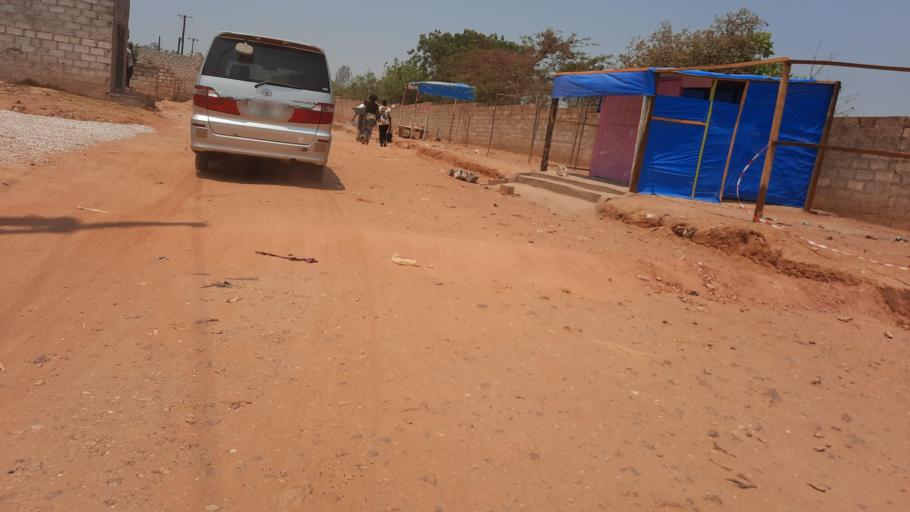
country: ZM
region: Lusaka
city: Lusaka
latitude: -15.4084
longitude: 28.3800
